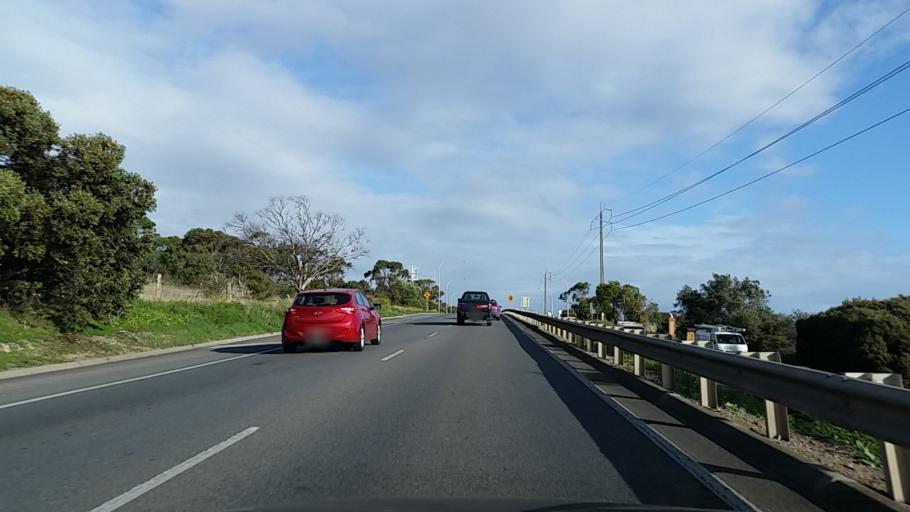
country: AU
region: South Australia
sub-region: Adelaide Hills
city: Seacliff
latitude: -35.0524
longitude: 138.5348
